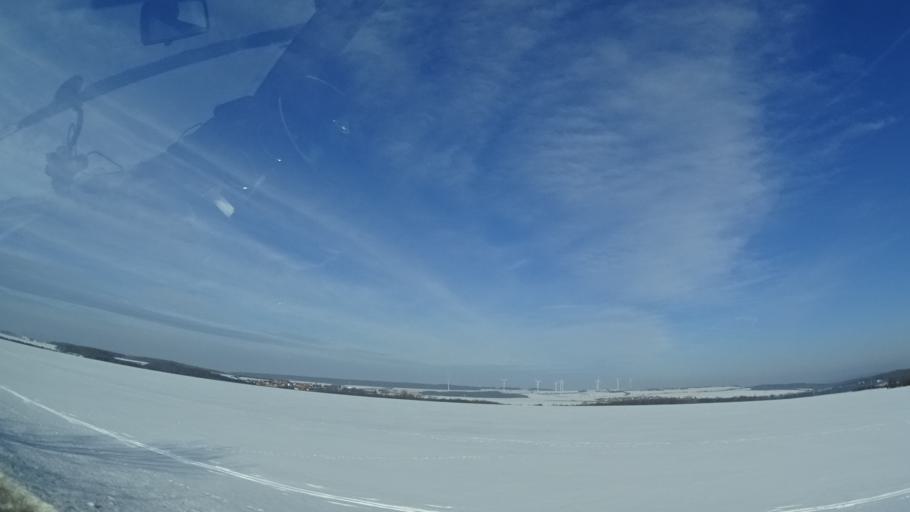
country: DE
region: Thuringia
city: Milda
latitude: 50.8566
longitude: 11.4942
